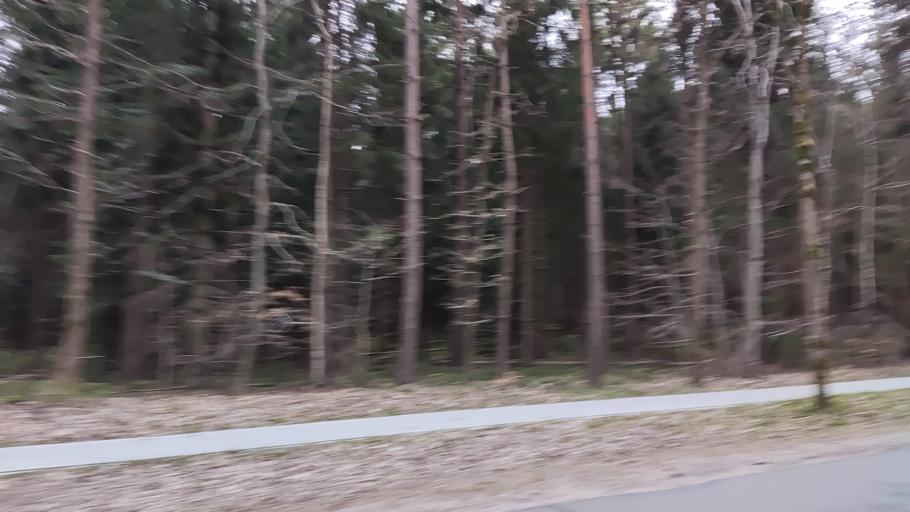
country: DE
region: Lower Saxony
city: Jesteburg
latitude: 53.2924
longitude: 9.9428
